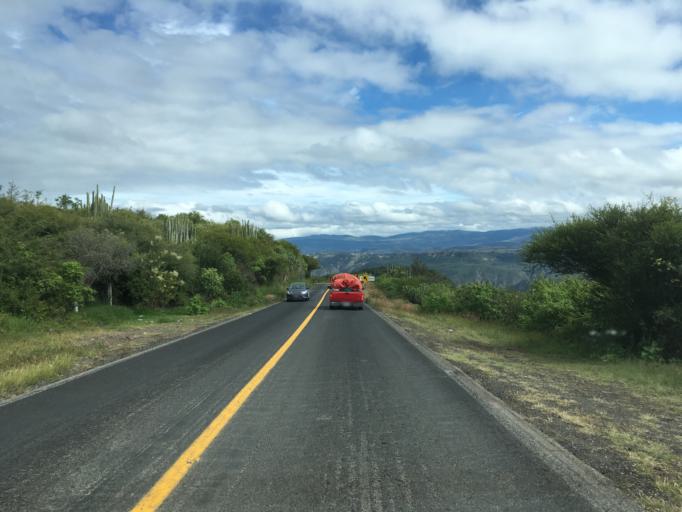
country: MX
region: Hidalgo
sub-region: Atotonilco el Grande
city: Santa Maria Amajac
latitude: 20.4091
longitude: -98.6949
